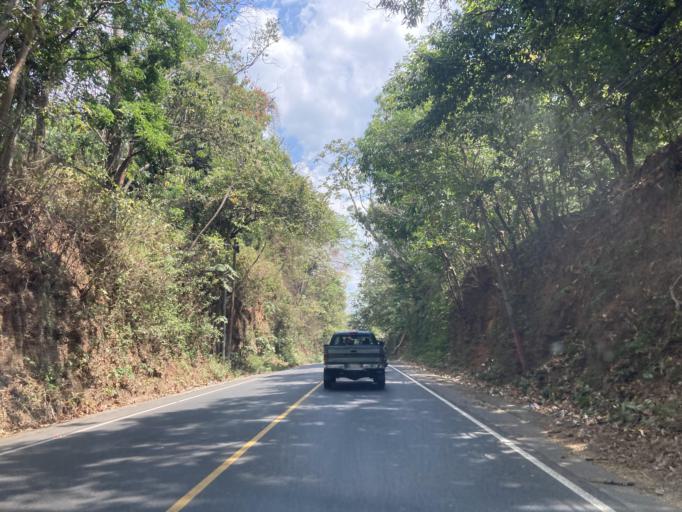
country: GT
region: Santa Rosa
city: Guazacapan
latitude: 14.0697
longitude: -90.4329
